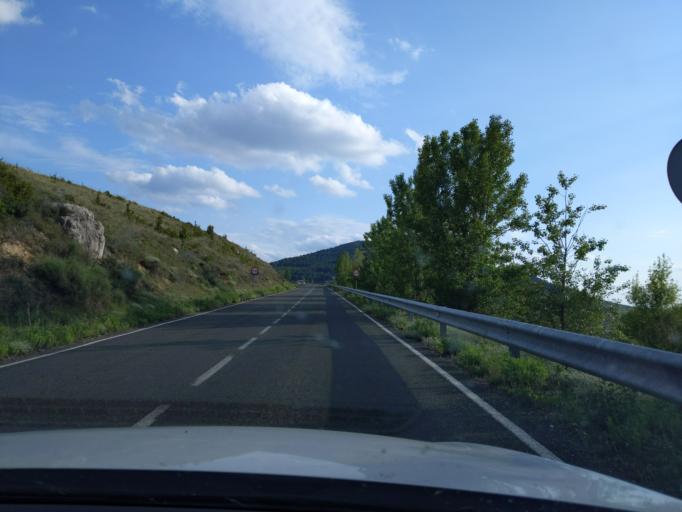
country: ES
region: La Rioja
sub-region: Provincia de La Rioja
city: Clavijo
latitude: 42.3619
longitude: -2.4253
